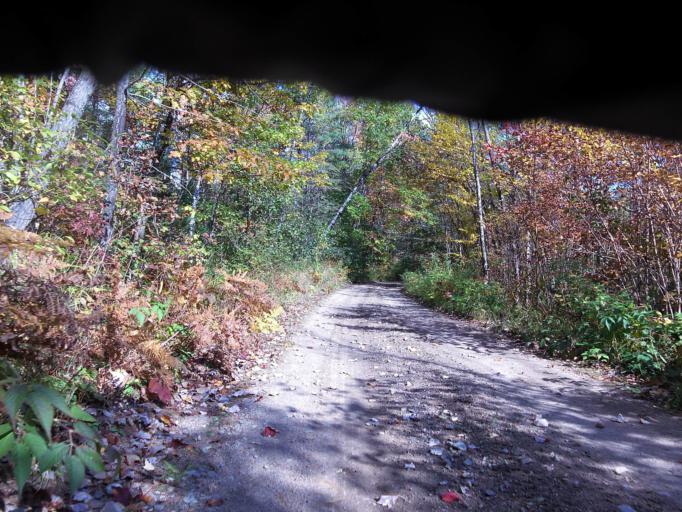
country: CA
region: Ontario
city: Petawawa
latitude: 45.8004
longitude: -77.3093
